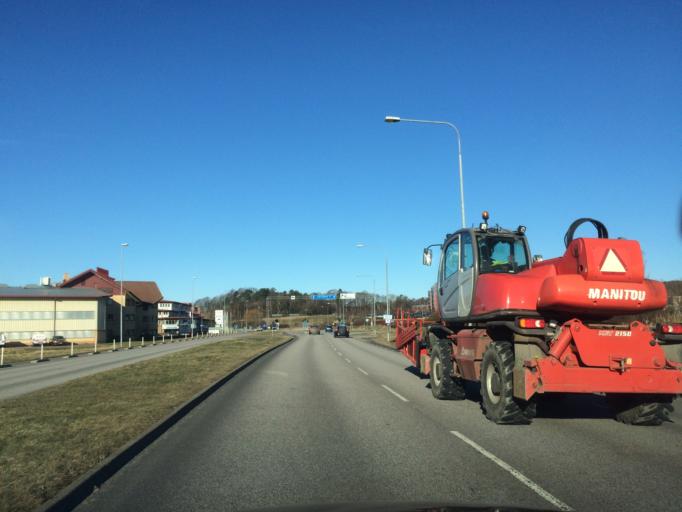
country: SE
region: Vaestra Goetaland
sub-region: Molndal
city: Moelndal
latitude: 57.6486
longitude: 11.9628
